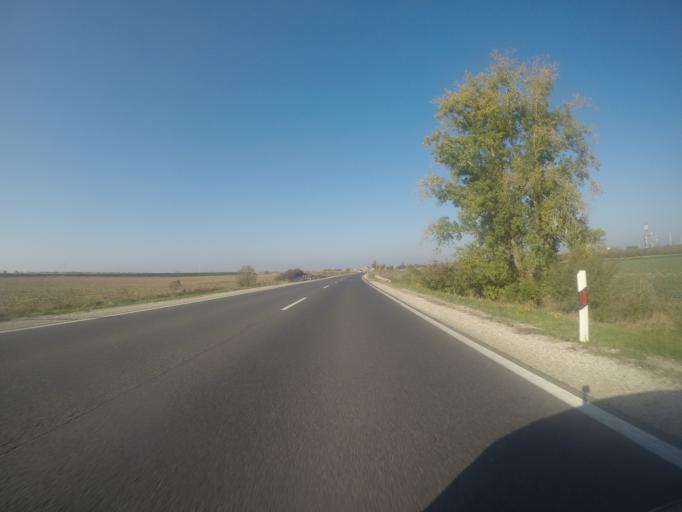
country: HU
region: Fejer
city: Ercsi
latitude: 47.2833
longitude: 18.8733
